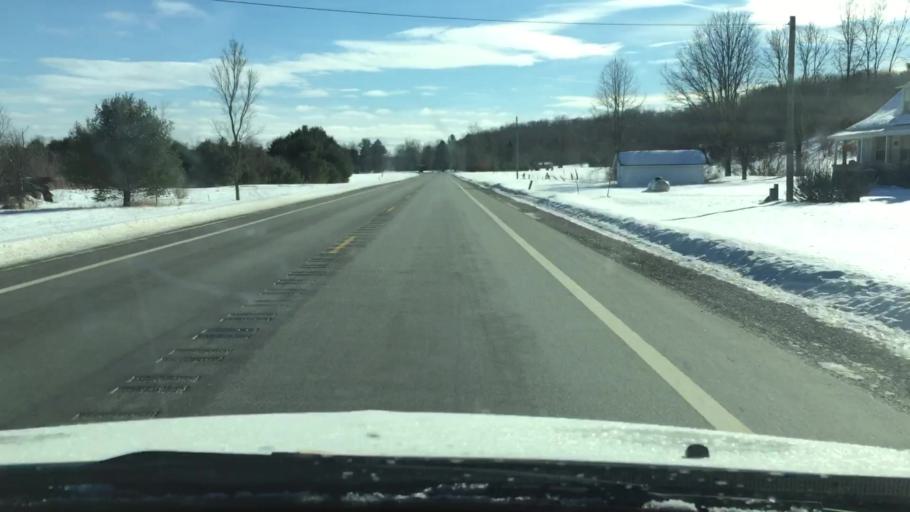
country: US
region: Michigan
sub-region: Charlevoix County
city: East Jordan
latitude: 45.0713
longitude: -85.0857
